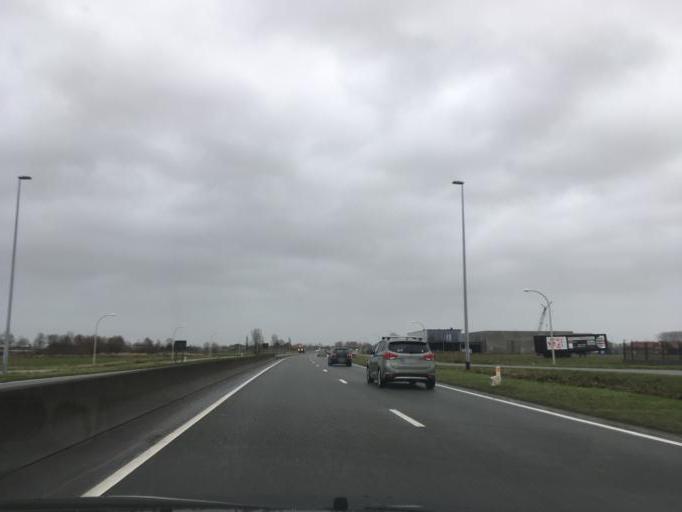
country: BE
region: Flanders
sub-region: Provincie West-Vlaanderen
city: Roeselare
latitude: 50.9812
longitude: 3.1335
